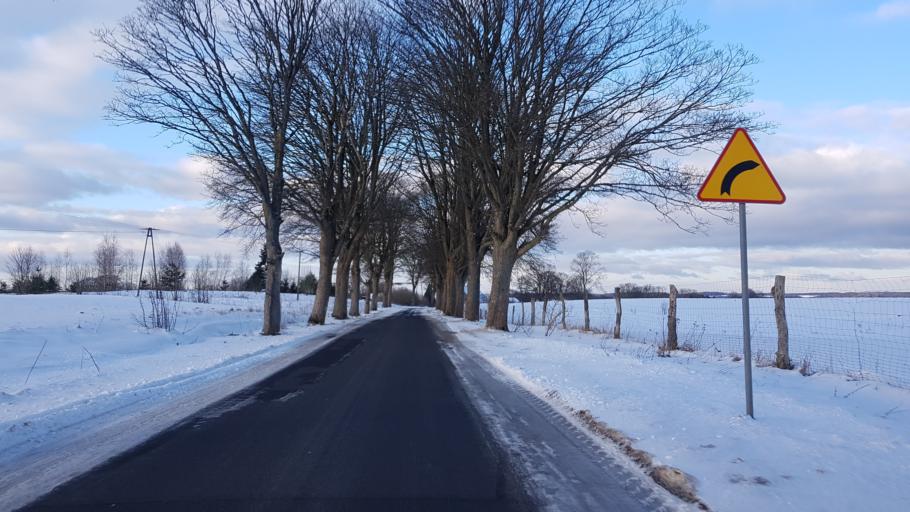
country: PL
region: West Pomeranian Voivodeship
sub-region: Powiat koszalinski
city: Bobolice
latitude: 53.9862
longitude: 16.6874
